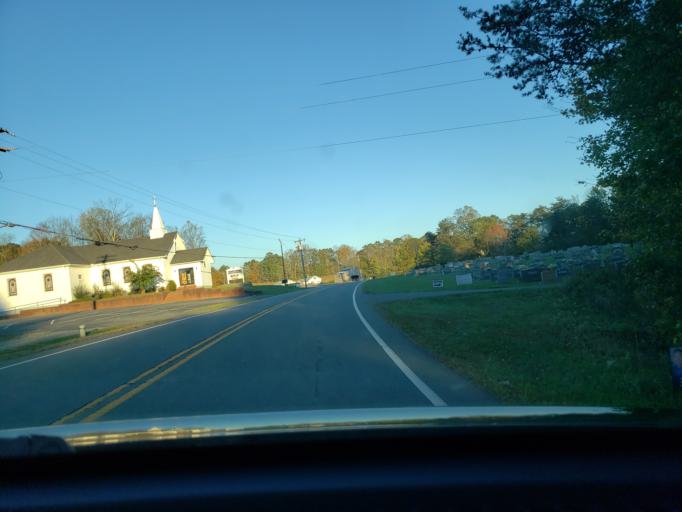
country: US
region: North Carolina
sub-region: Stokes County
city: Danbury
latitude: 36.3224
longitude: -80.2321
